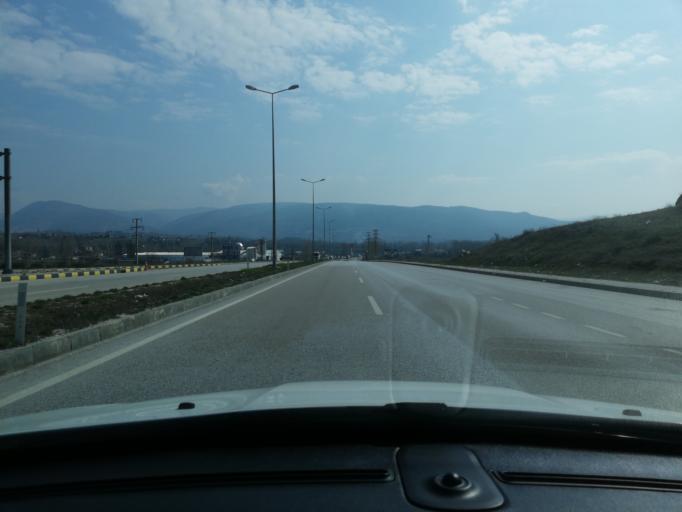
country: TR
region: Cankiri
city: Ilgaz
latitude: 40.9076
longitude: 33.6224
